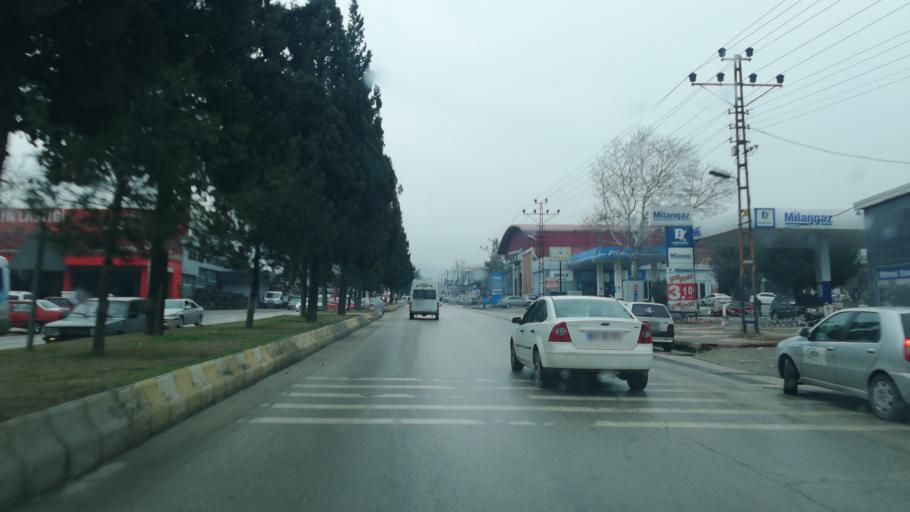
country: TR
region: Kahramanmaras
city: Kahramanmaras
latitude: 37.5637
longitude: 36.9594
